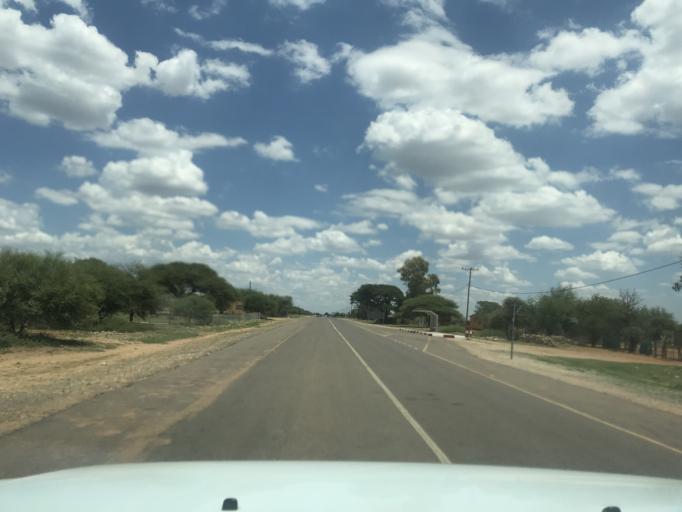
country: BW
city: Mabuli
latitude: -25.7346
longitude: 25.1072
